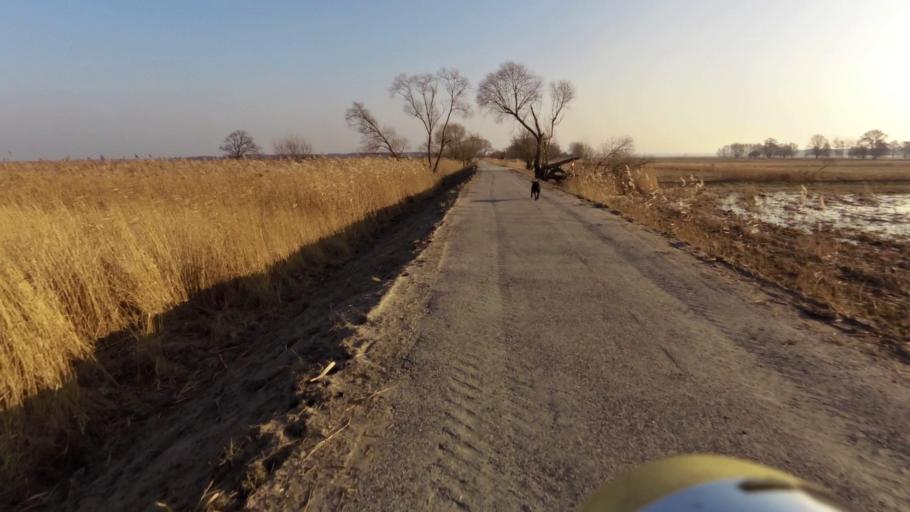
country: PL
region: West Pomeranian Voivodeship
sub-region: Powiat kamienski
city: Wolin
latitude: 53.7562
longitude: 14.5690
